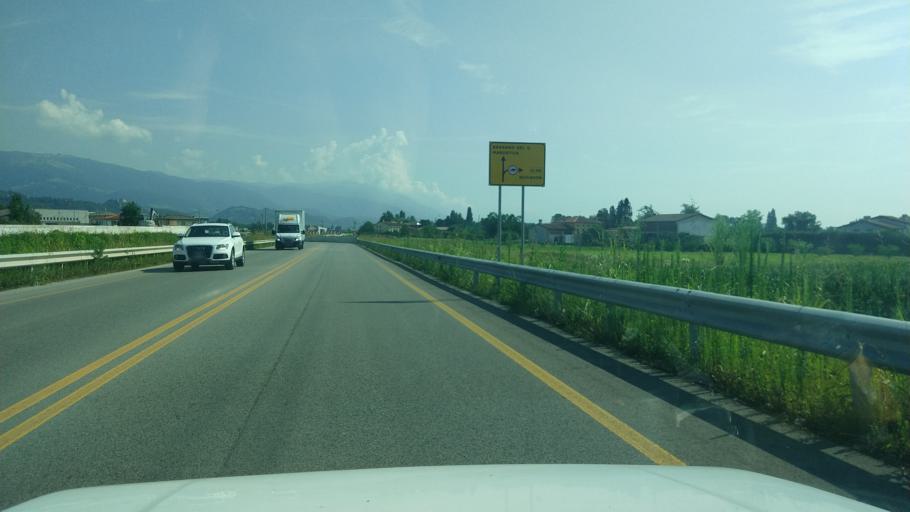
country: IT
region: Veneto
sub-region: Provincia di Vicenza
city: Schiavon
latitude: 45.7124
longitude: 11.6336
